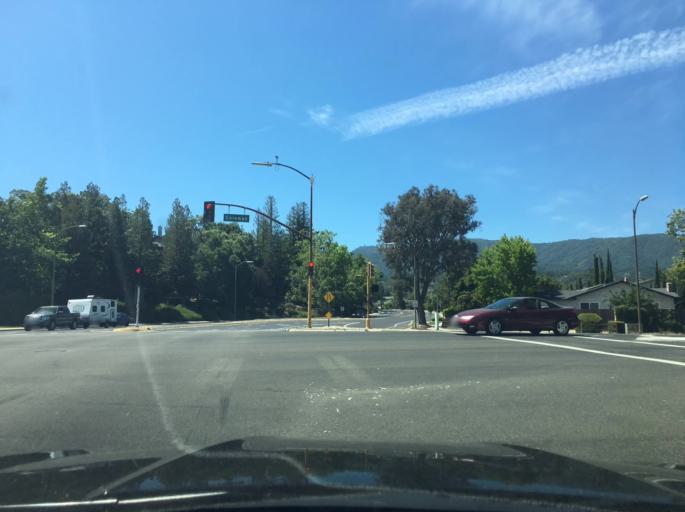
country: US
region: California
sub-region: Santa Clara County
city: Cambrian Park
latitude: 37.2380
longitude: -121.8868
